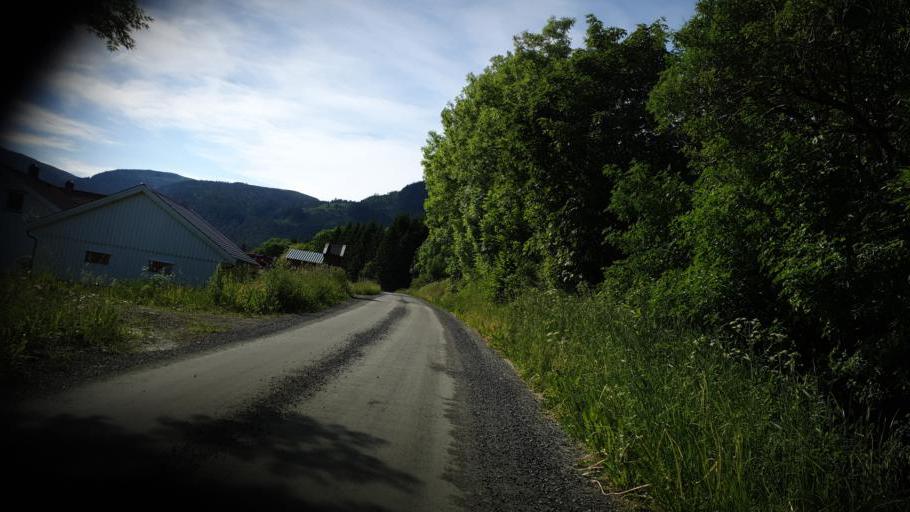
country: NO
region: Sor-Trondelag
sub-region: Trondheim
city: Trondheim
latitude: 63.5750
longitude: 10.3926
